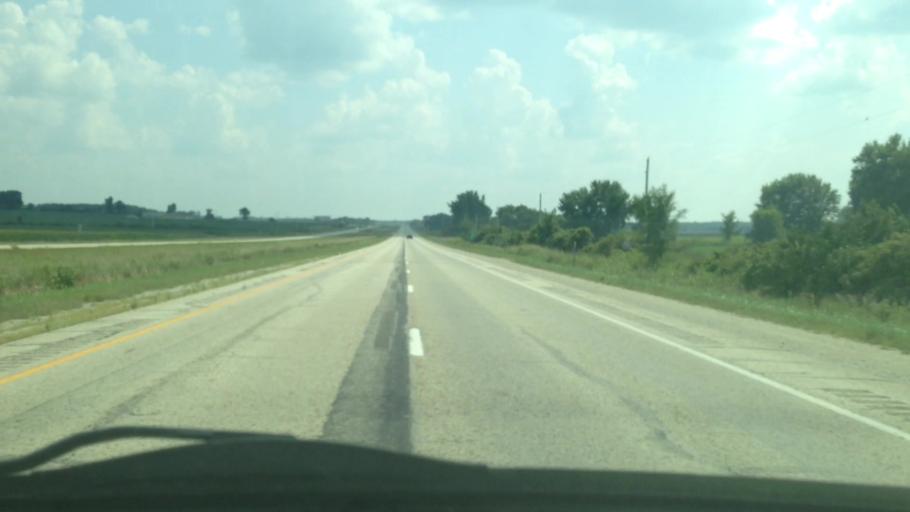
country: US
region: Iowa
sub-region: Bremer County
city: Tripoli
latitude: 42.9265
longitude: -92.3176
